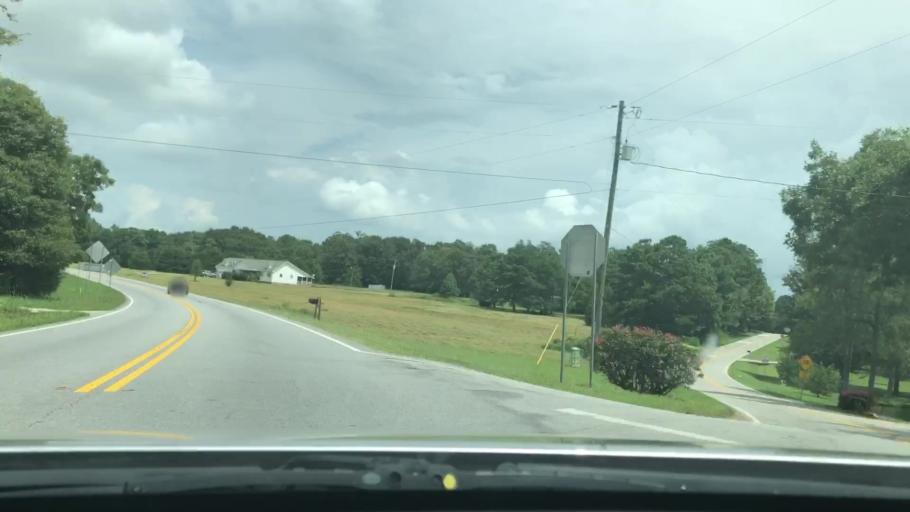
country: US
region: Georgia
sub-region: Lamar County
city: Barnesville
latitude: 33.1546
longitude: -84.1140
